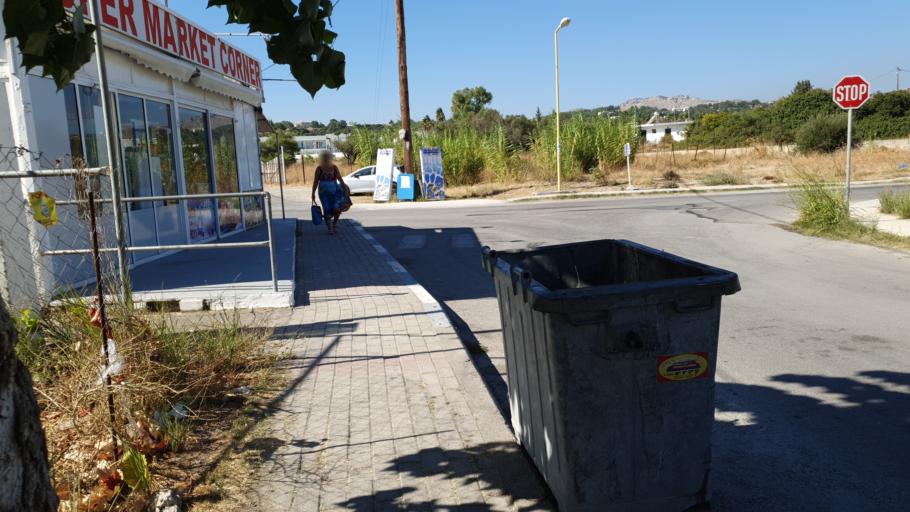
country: GR
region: South Aegean
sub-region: Nomos Dodekanisou
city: Faliraki
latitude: 36.3319
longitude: 28.2071
